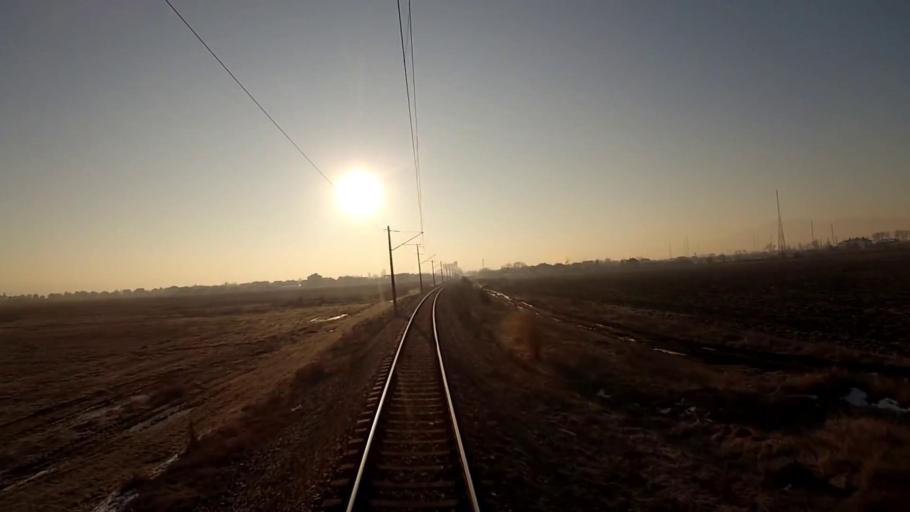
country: BG
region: Sofiya
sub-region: Obshtina Kostinbrod
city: Kostinbrod
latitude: 42.8074
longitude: 23.1991
